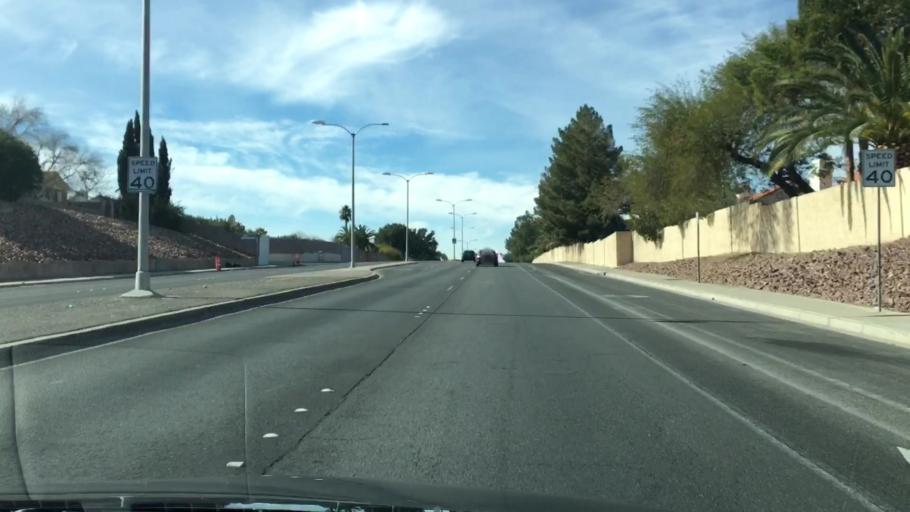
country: US
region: Nevada
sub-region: Clark County
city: Whitney
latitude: 36.0562
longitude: -115.0613
